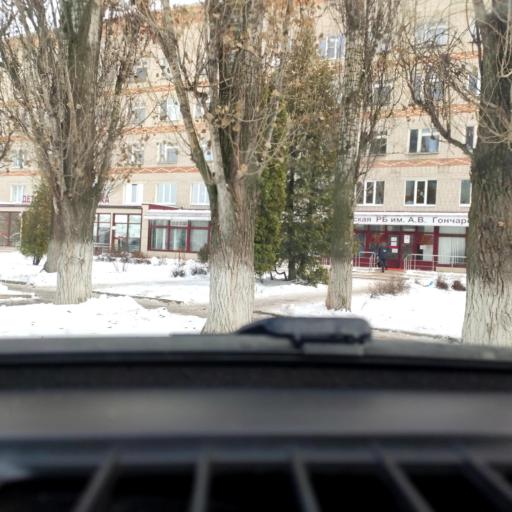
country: RU
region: Voronezj
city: Semiluki
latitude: 51.7008
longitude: 39.0228
